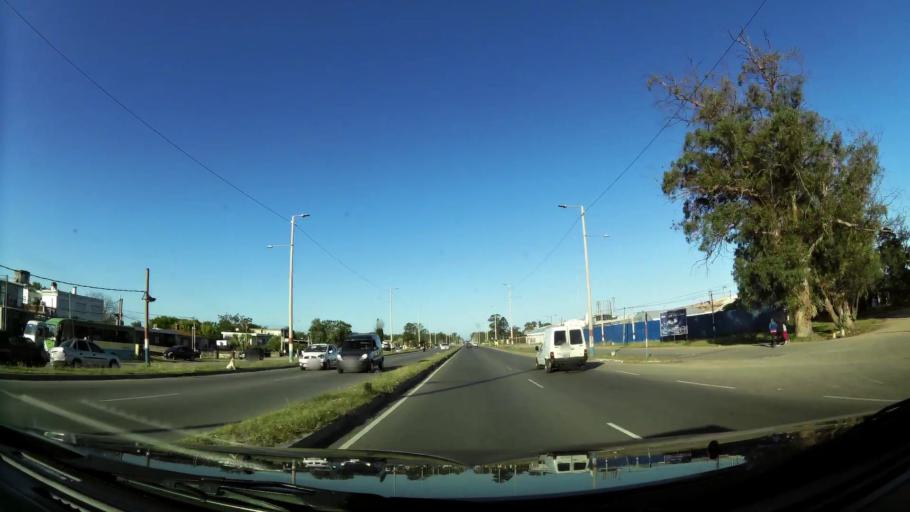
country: UY
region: Canelones
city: Paso de Carrasco
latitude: -34.8596
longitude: -56.0500
